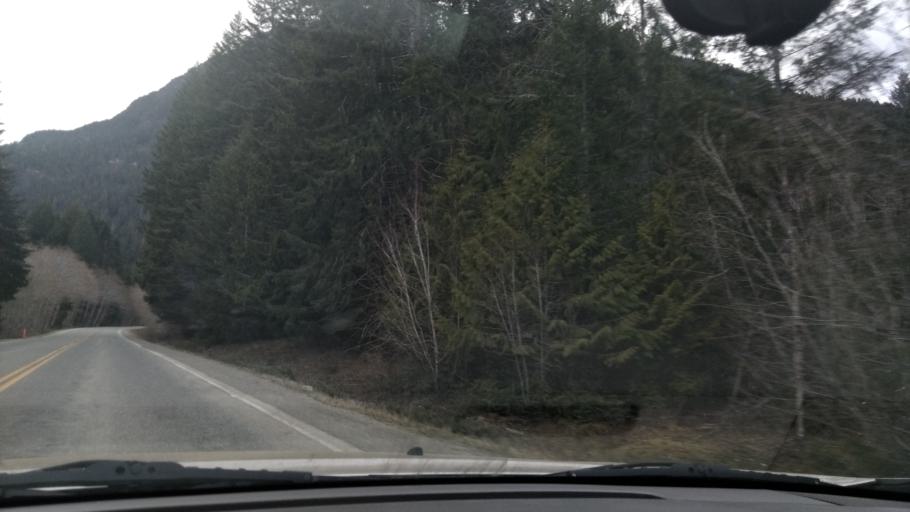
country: CA
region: British Columbia
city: Campbell River
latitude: 49.8538
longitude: -125.8296
